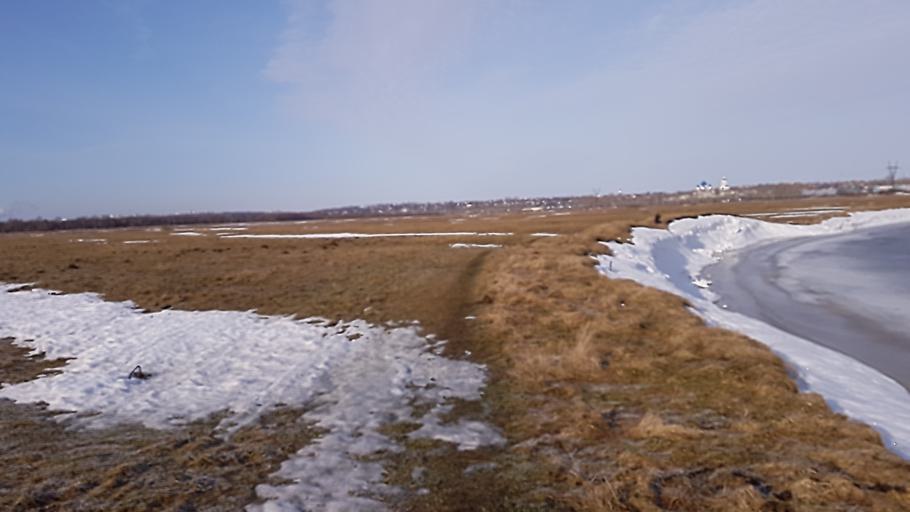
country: RU
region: Vladimir
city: Bogolyubovo
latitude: 56.1907
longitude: 40.5678
